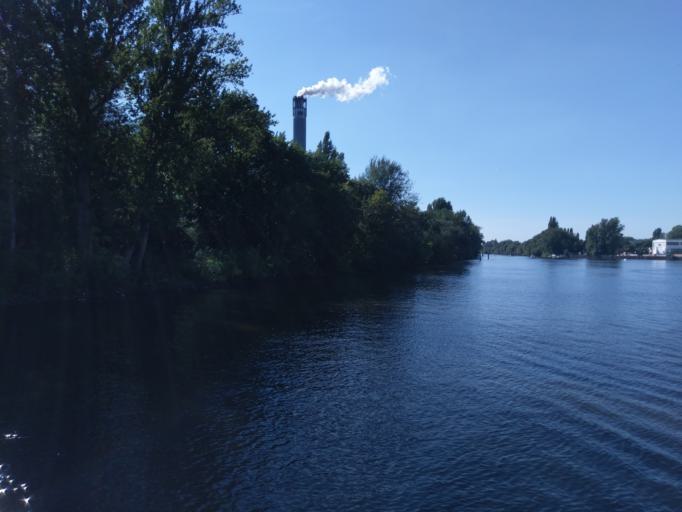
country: DE
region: Berlin
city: Haselhorst
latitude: 52.5337
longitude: 13.2352
